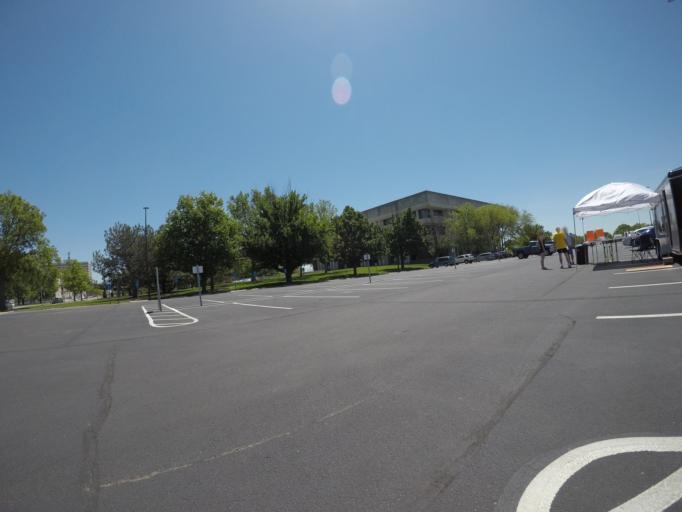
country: US
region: Kansas
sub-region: Shawnee County
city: Topeka
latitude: 39.0466
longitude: -95.6797
